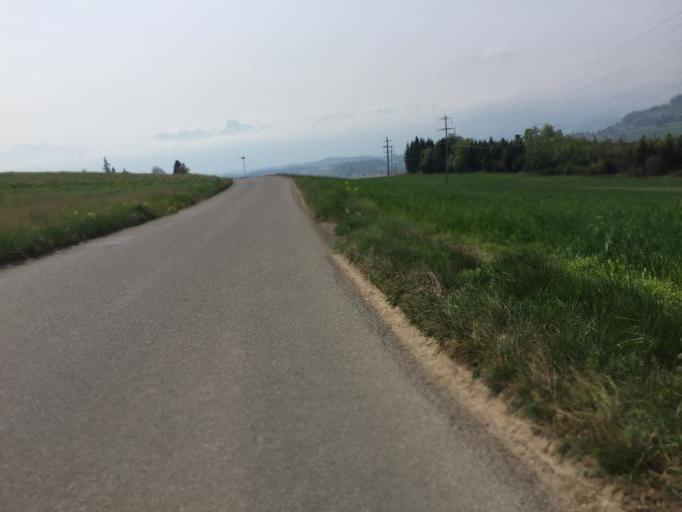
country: CH
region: Bern
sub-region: Bern-Mittelland District
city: Taegertschi
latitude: 46.8657
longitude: 7.5815
